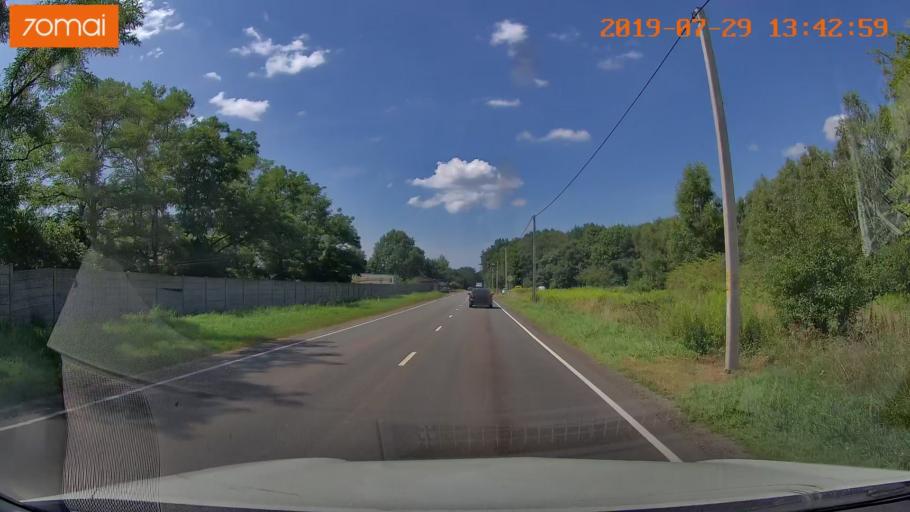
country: RU
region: Kaliningrad
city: Svetlyy
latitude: 54.7370
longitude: 20.1032
